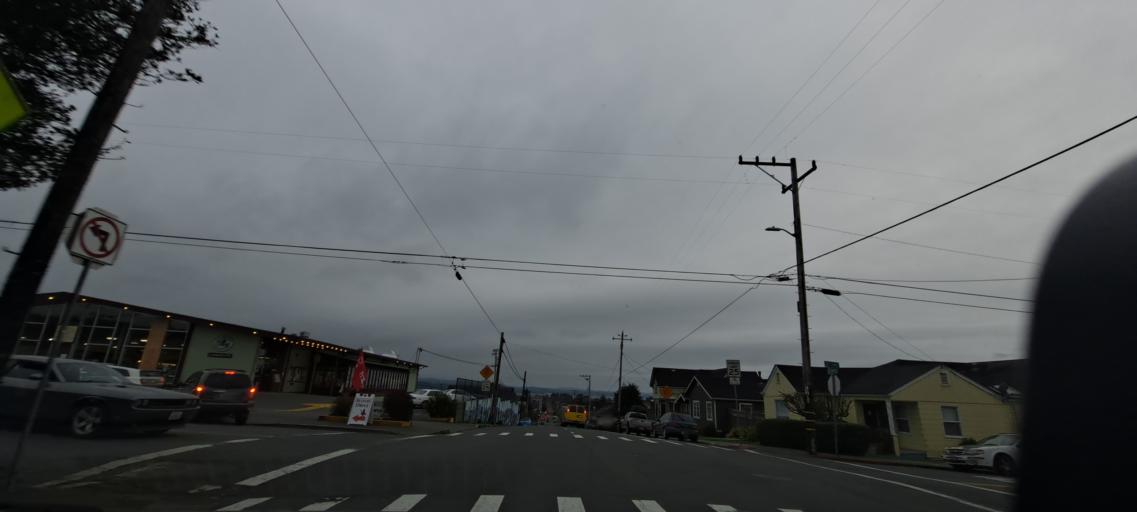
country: US
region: California
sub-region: Humboldt County
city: Arcata
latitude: 40.8723
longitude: -124.0856
